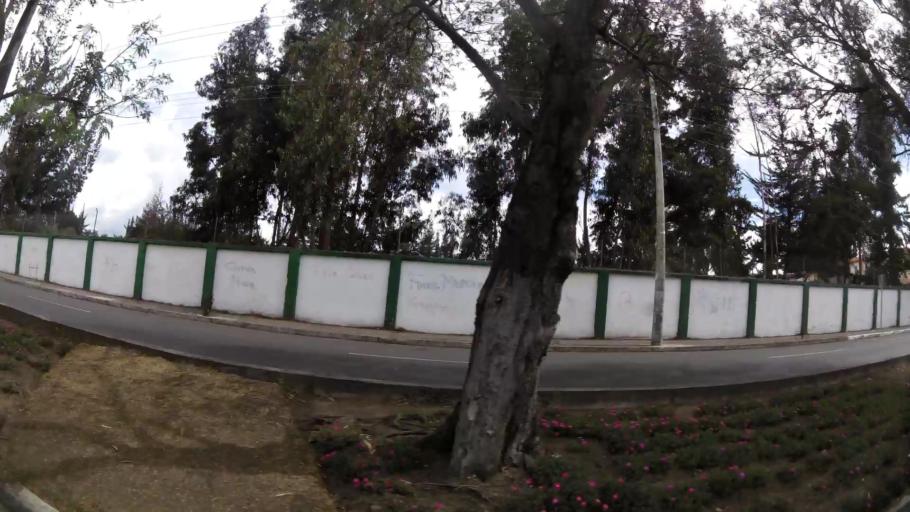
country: EC
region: Tungurahua
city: Ambato
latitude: -1.2529
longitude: -78.6286
